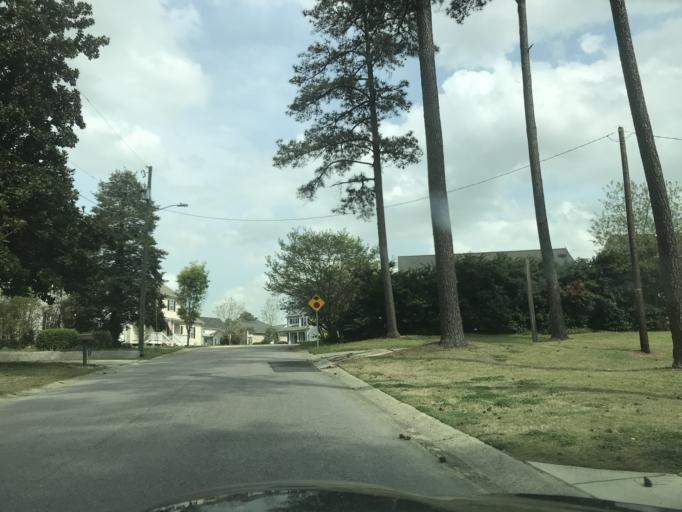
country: US
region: North Carolina
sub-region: Wake County
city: Raleigh
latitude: 35.8220
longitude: -78.5841
